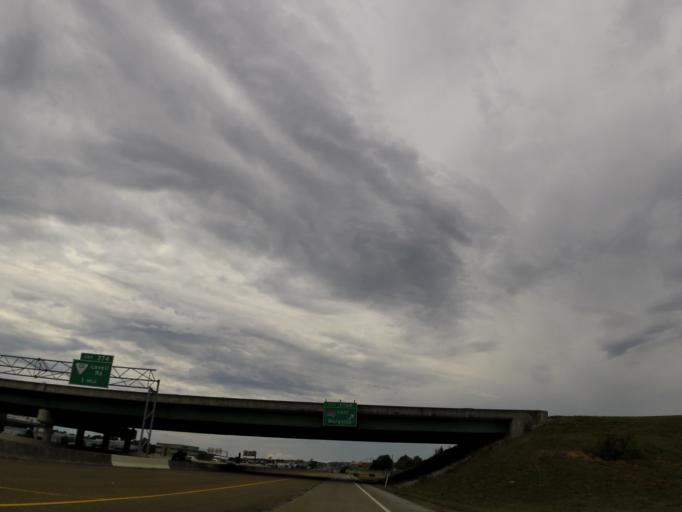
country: US
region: Tennessee
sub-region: Knox County
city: Farragut
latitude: 35.9118
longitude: -84.1210
